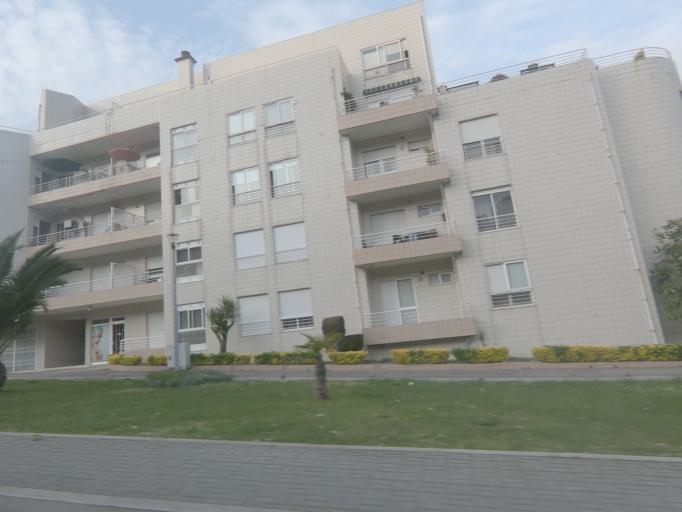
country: PT
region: Porto
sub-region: Valongo
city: Valongo
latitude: 41.1922
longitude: -8.5141
